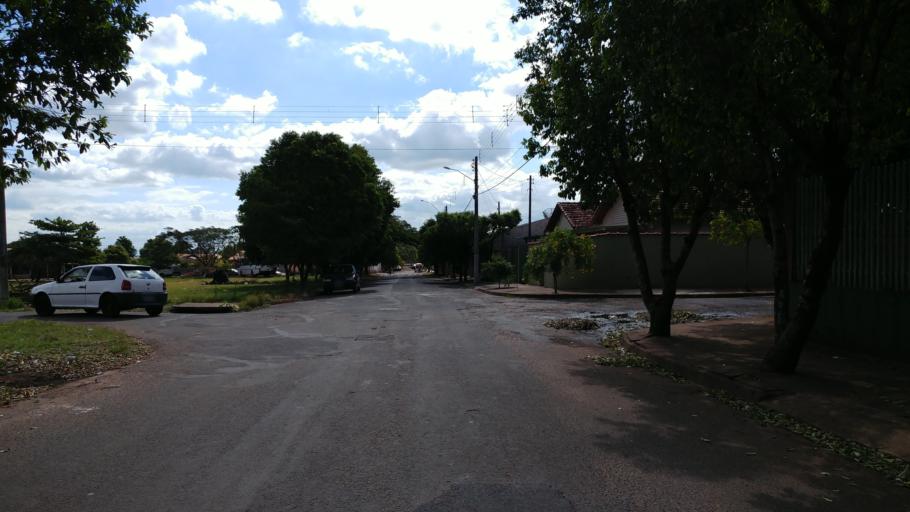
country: BR
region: Sao Paulo
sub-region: Paraguacu Paulista
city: Paraguacu Paulista
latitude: -22.4206
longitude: -50.5873
